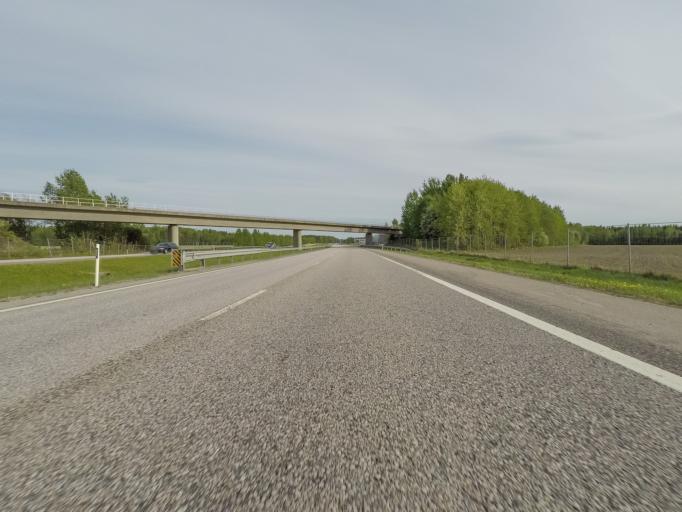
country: FI
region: Uusimaa
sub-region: Helsinki
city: Hyvinge
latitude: 60.5808
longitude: 24.8029
